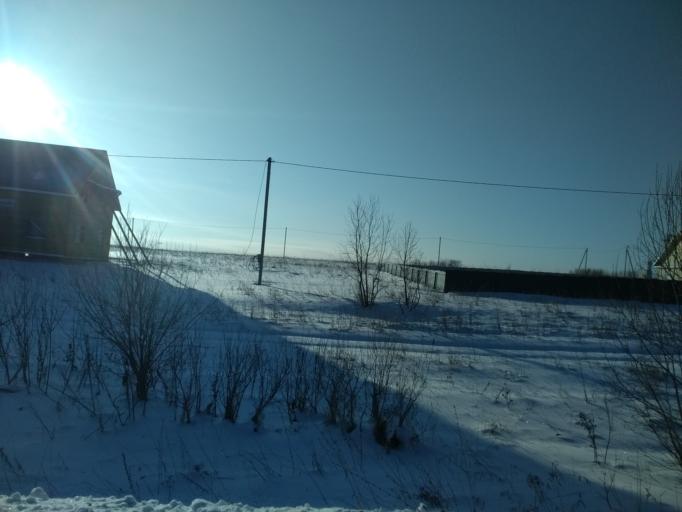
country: RU
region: Bashkortostan
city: Iglino
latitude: 54.6846
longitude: 56.6036
